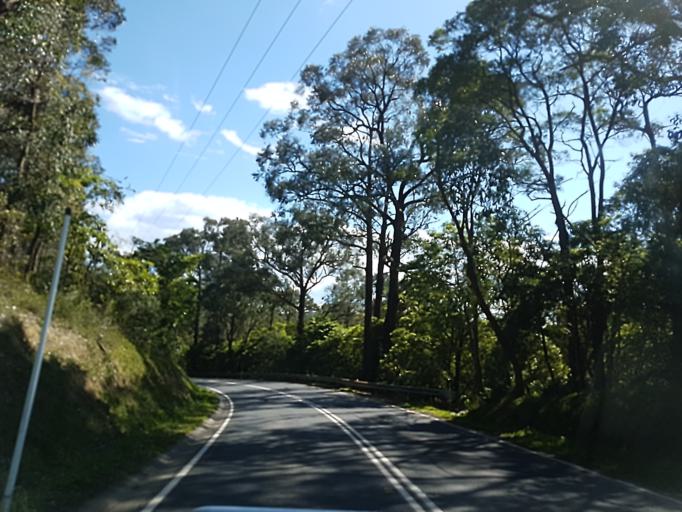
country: AU
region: Victoria
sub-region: Cardinia
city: Pakenham Upper
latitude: -38.0115
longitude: 145.5124
